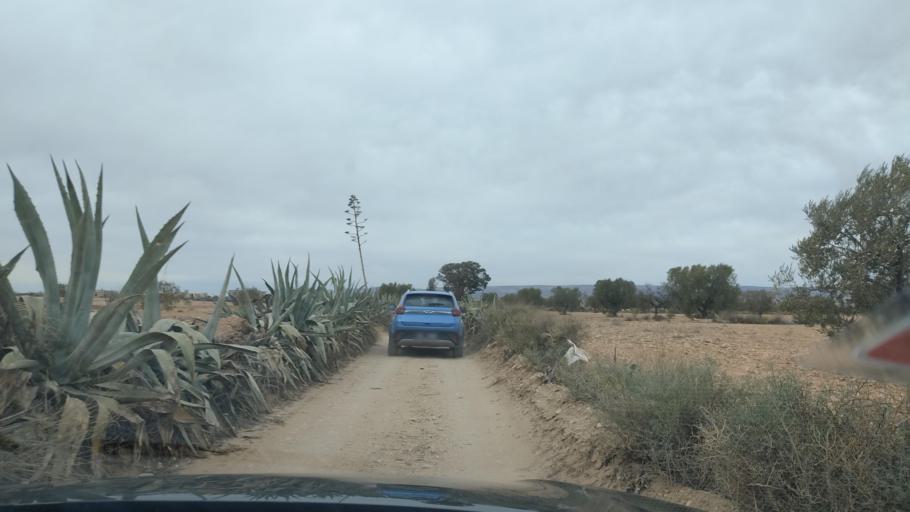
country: TN
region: Al Qasrayn
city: Kasserine
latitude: 35.2276
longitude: 8.9310
